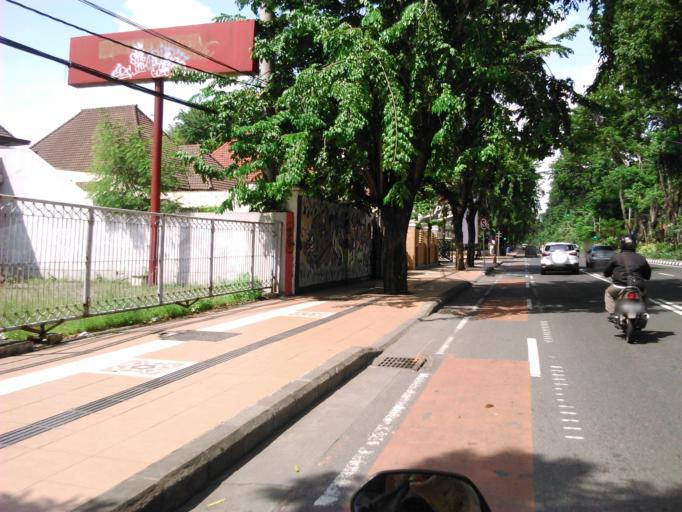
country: ID
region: East Java
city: Gubengairlangga
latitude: -7.2864
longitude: 112.7398
